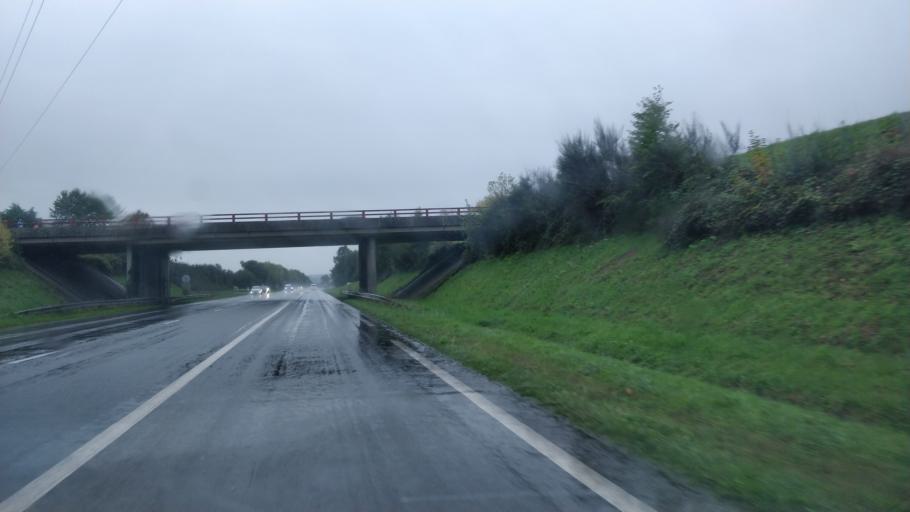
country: FR
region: Lower Normandy
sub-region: Departement de la Manche
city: Saint-Planchers
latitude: 48.8381
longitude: -1.5390
